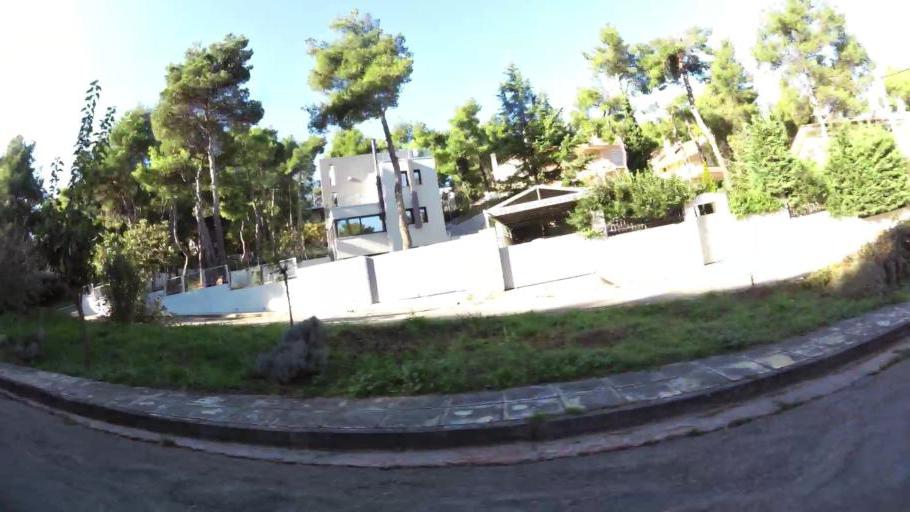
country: GR
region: Attica
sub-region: Nomarchia Anatolikis Attikis
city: Stamata
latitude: 38.1347
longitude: 23.8769
